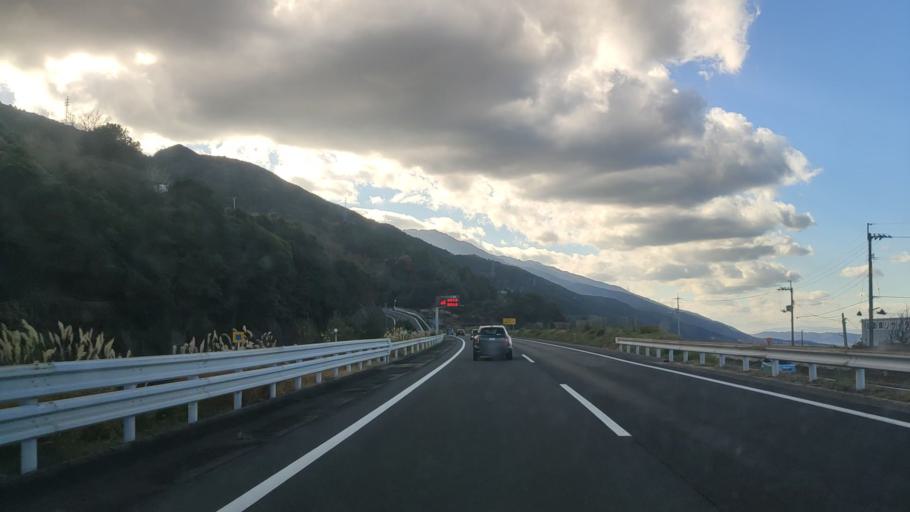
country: JP
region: Ehime
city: Kawanoecho
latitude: 33.9679
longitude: 133.5442
